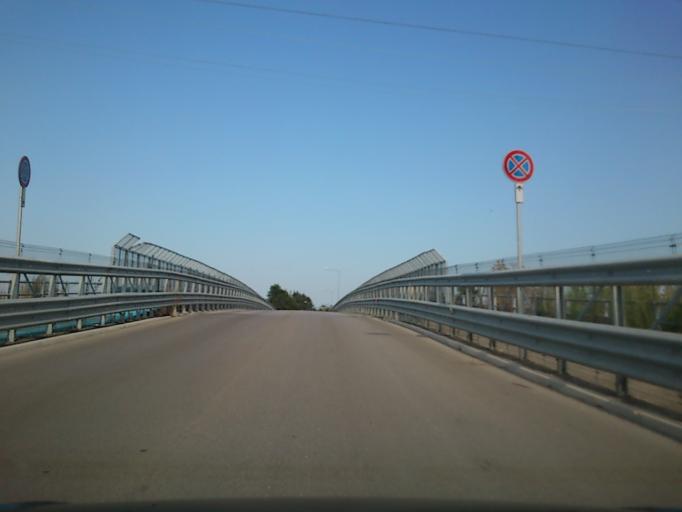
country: IT
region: The Marches
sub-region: Provincia di Pesaro e Urbino
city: Centinarola
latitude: 43.8311
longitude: 12.9941
